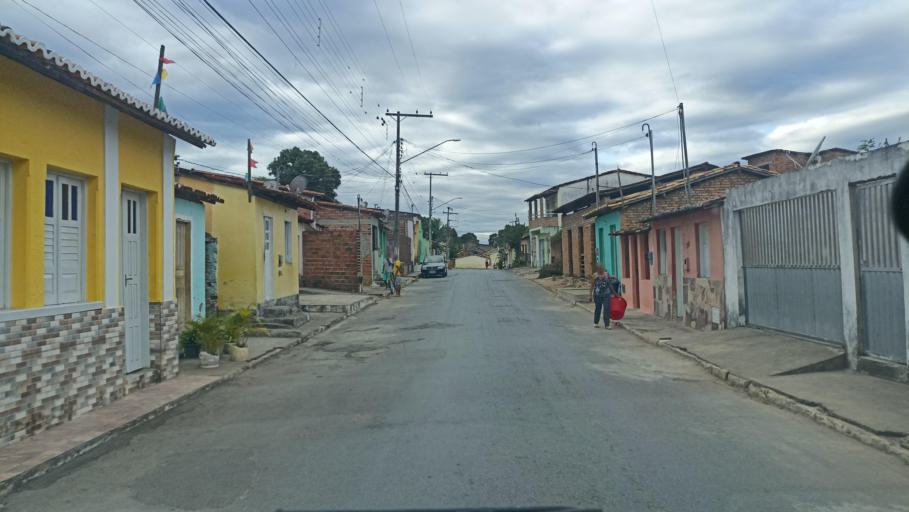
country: BR
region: Bahia
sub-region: Andarai
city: Vera Cruz
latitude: -12.8123
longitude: -41.3320
